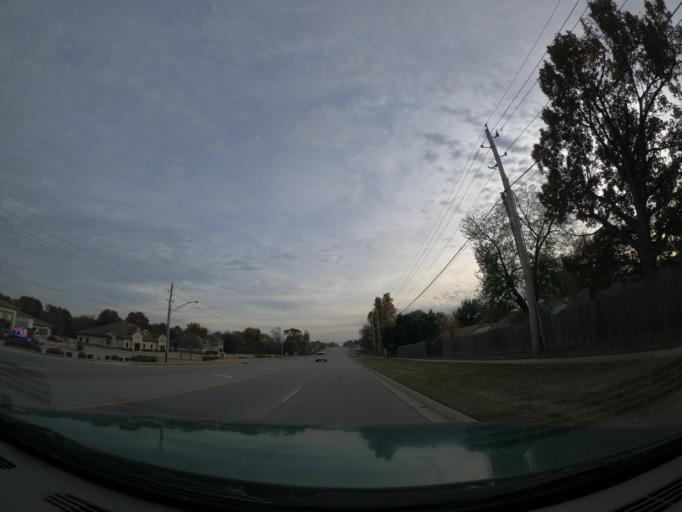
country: US
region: Oklahoma
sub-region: Tulsa County
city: Broken Arrow
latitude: 36.0504
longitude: -95.8154
